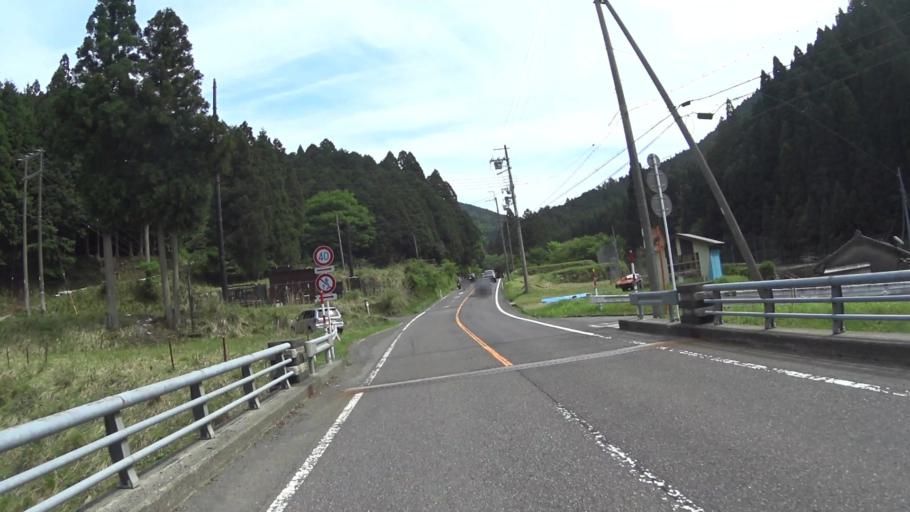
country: JP
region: Shiga Prefecture
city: Kitahama
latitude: 35.2017
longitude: 135.8595
